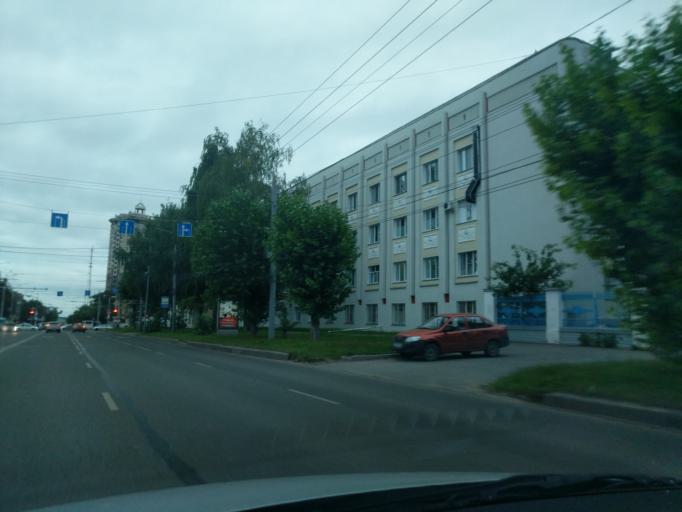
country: RU
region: Kirov
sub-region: Kirovo-Chepetskiy Rayon
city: Kirov
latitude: 58.5938
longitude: 49.6665
